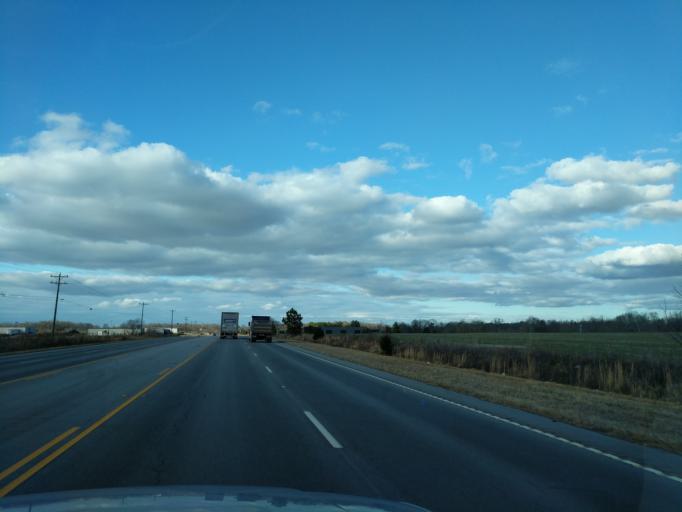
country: US
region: South Carolina
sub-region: Greenville County
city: Five Forks
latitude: 34.8349
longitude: -82.1446
